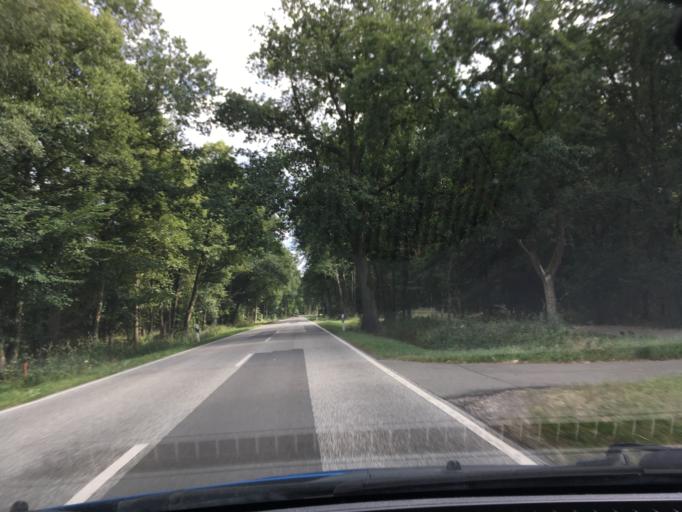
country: DE
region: Mecklenburg-Vorpommern
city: Lubtheen
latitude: 53.3572
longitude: 11.0856
